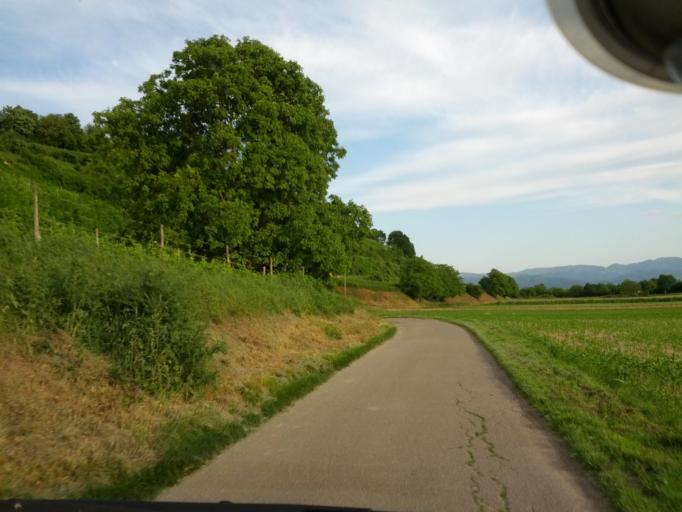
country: DE
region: Baden-Wuerttemberg
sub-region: Freiburg Region
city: Merdingen
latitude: 47.9738
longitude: 7.6754
